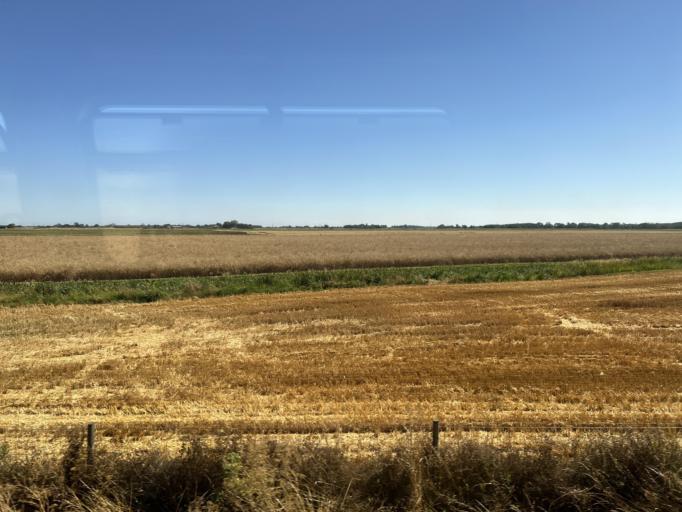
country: GB
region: England
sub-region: Lincolnshire
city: Spilsby
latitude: 53.1215
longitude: 0.1379
